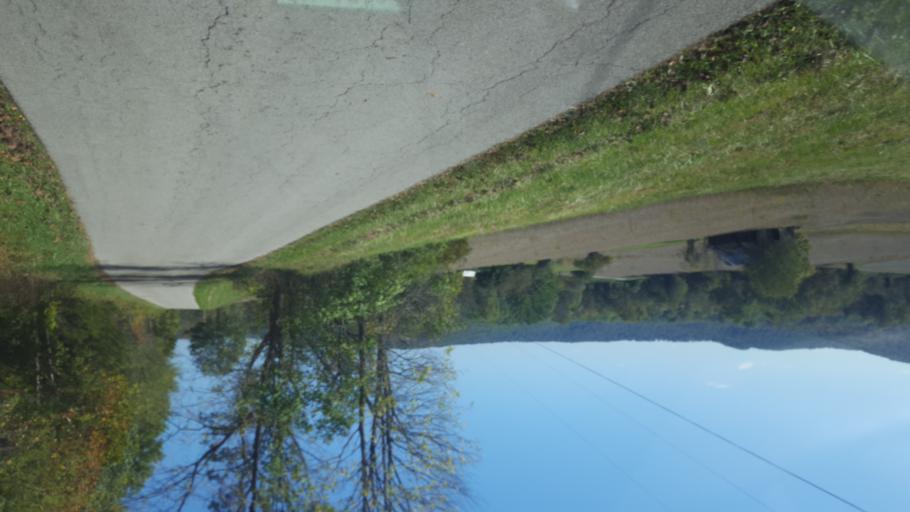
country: US
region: Kentucky
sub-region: Fleming County
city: Flemingsburg
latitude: 38.4451
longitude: -83.5708
